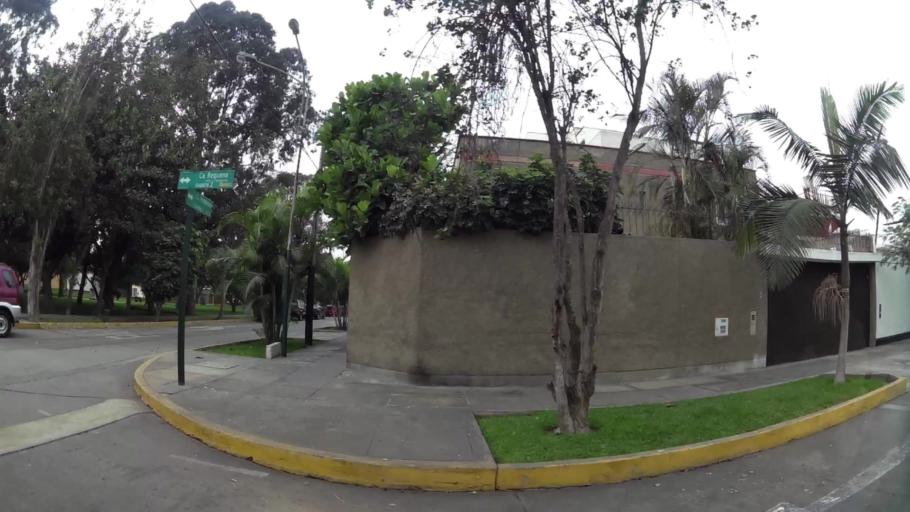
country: PE
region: Lima
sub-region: Lima
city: Surco
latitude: -12.1208
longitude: -76.9928
